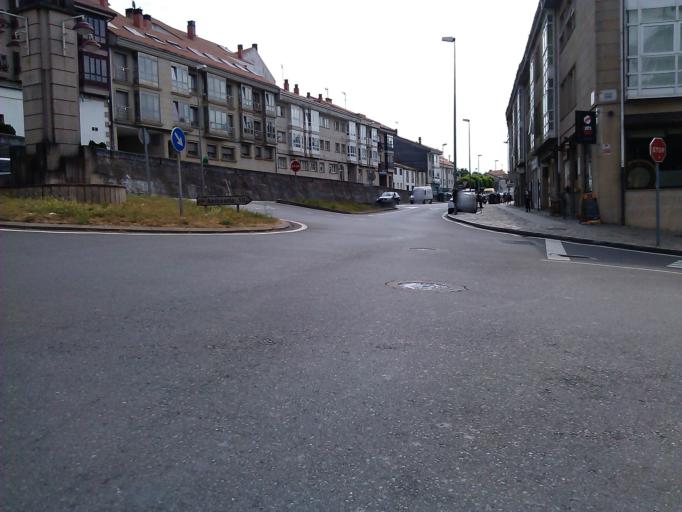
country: ES
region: Galicia
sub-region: Provincia da Coruna
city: Santiago de Compostela
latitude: 42.8873
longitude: -8.5238
